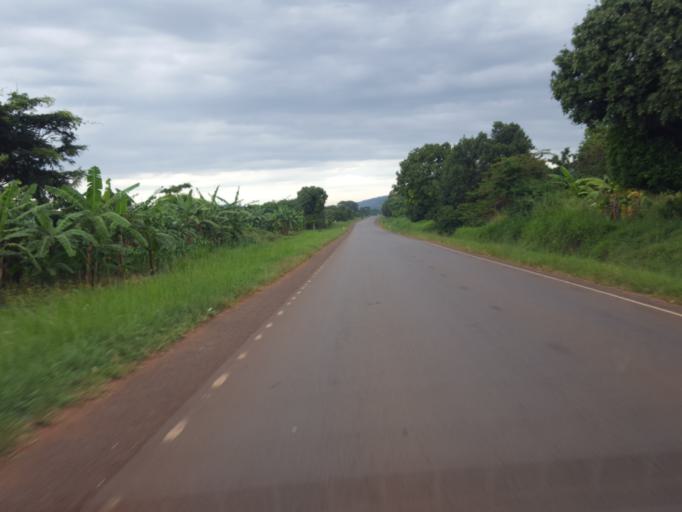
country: UG
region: Central Region
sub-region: Kiboga District
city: Kiboga
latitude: 0.8600
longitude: 31.8632
